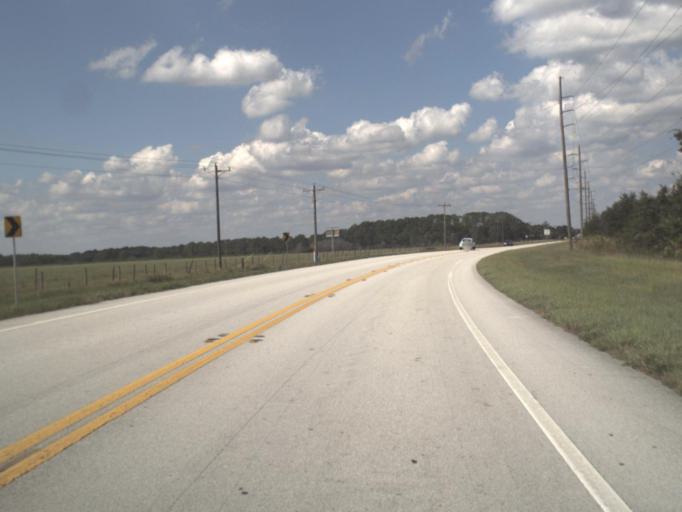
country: US
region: Florida
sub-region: Highlands County
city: Lake Placid
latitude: 27.4381
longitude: -81.2419
